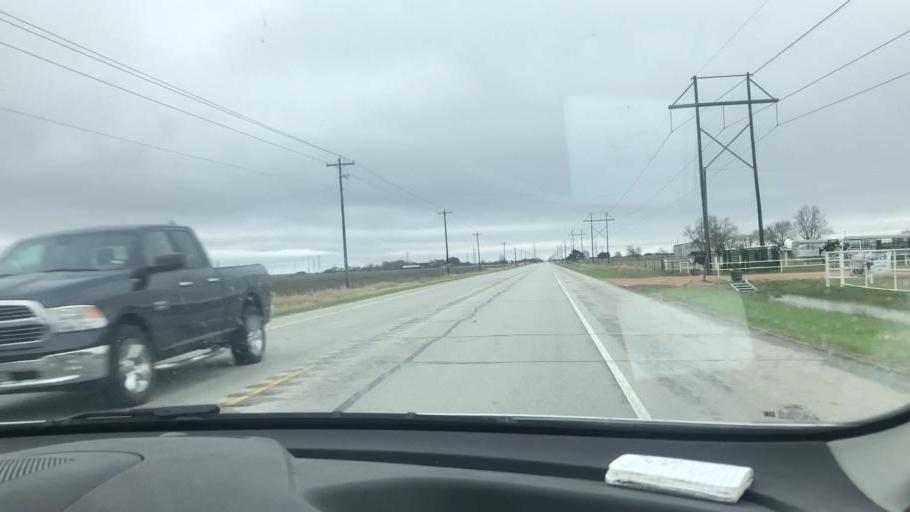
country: US
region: Texas
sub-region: Wharton County
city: Boling
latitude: 29.1894
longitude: -96.0136
